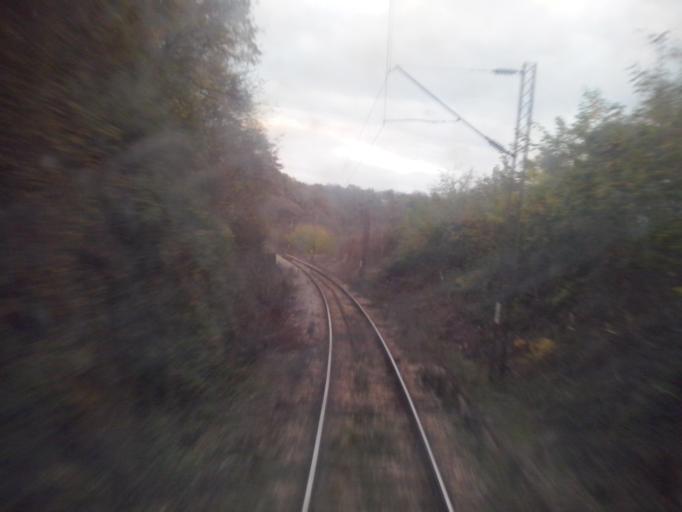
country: RS
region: Central Serbia
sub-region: Kolubarski Okrug
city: Valjevo
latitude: 44.2502
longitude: 19.8833
